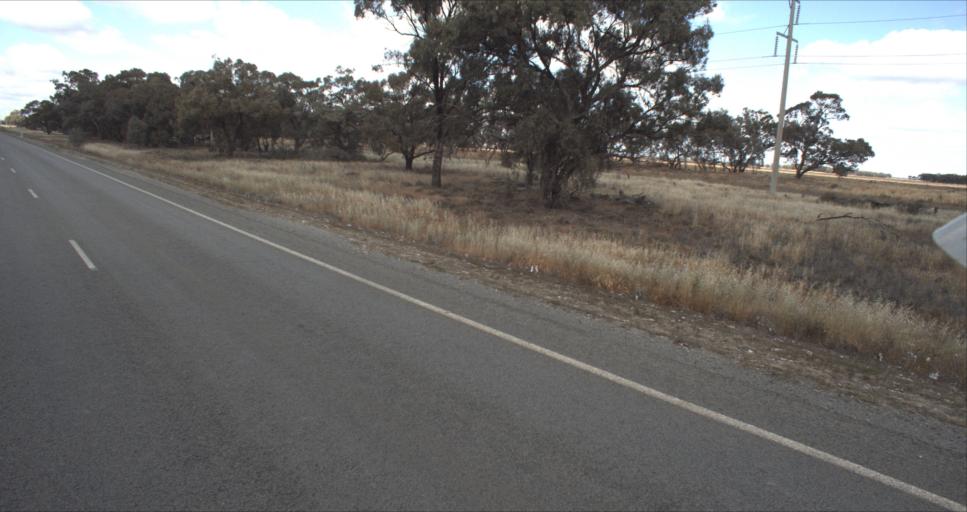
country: AU
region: New South Wales
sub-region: Murrumbidgee Shire
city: Darlington Point
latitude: -34.5710
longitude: 146.1672
